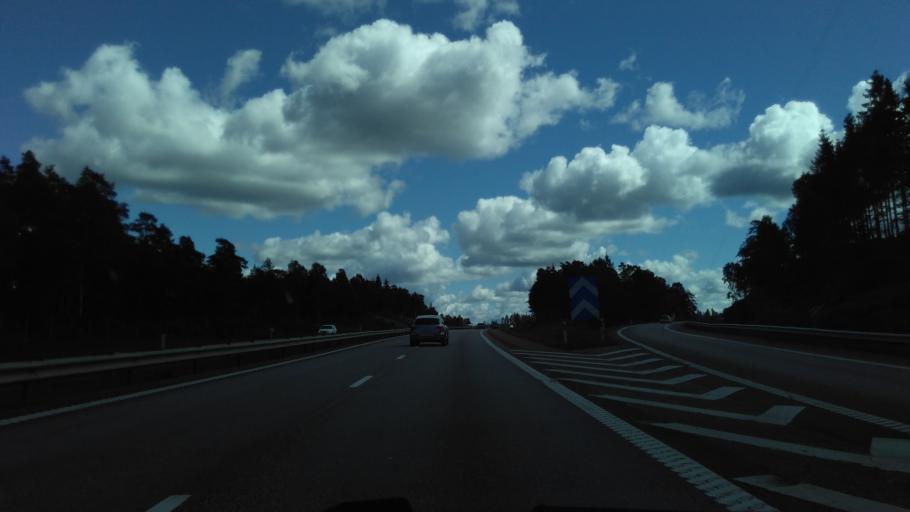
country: SE
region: Vaestra Goetaland
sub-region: Harryda Kommun
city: Landvetter
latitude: 57.6836
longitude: 12.3033
